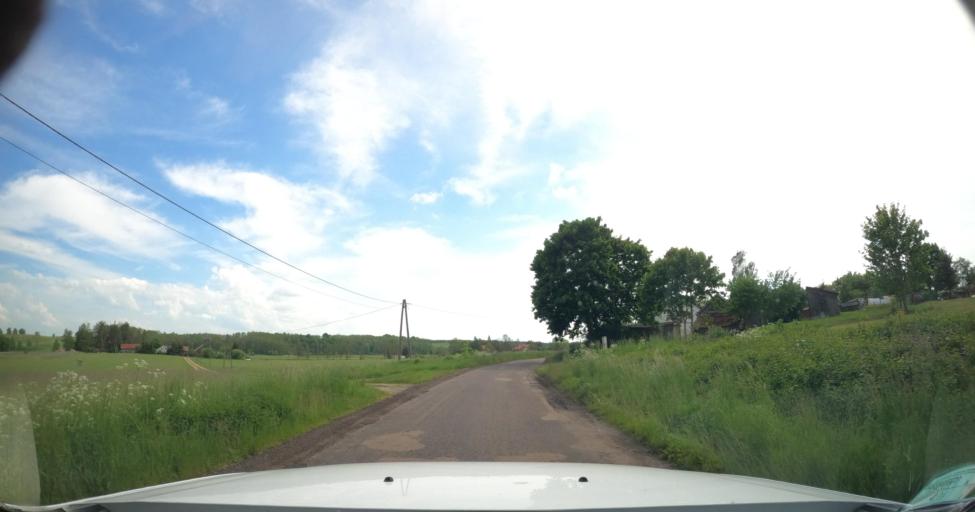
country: PL
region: Warmian-Masurian Voivodeship
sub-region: Powiat lidzbarski
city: Lidzbark Warminski
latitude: 54.1037
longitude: 20.4627
